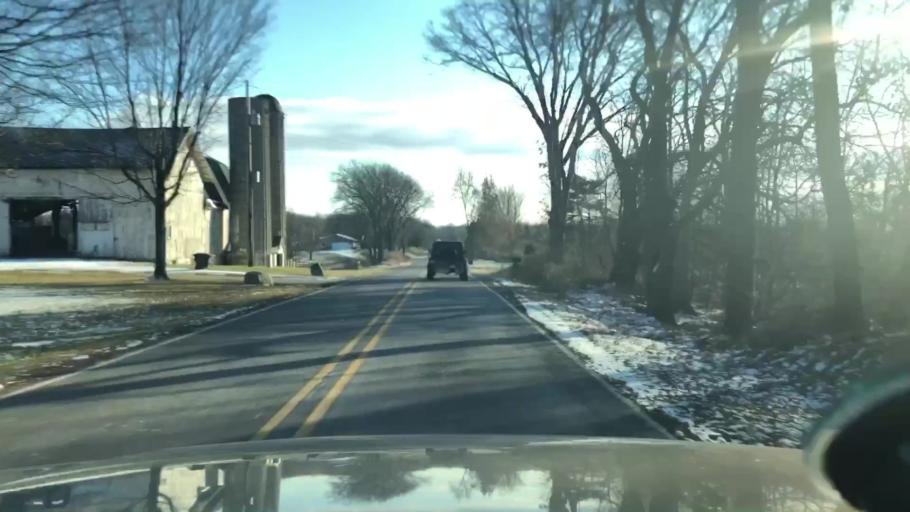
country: US
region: Michigan
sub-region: Jackson County
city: Vandercook Lake
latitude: 42.1206
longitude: -84.4514
